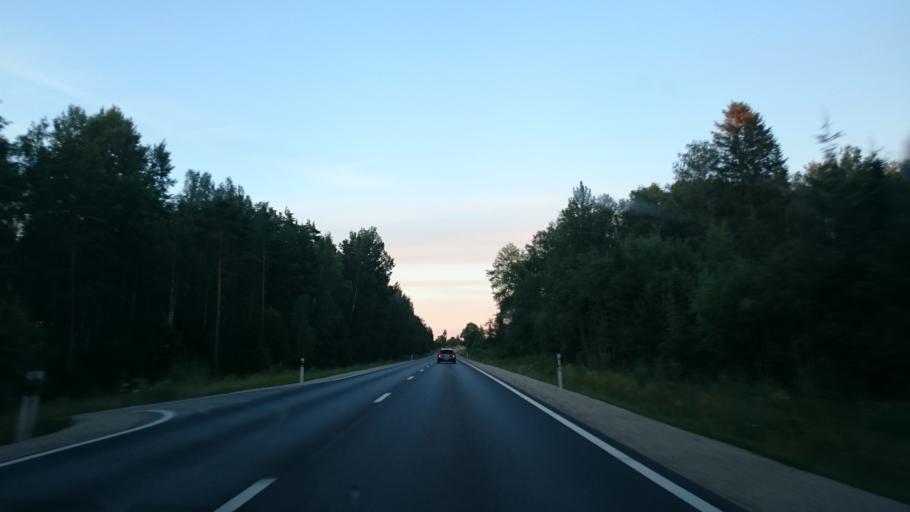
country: LV
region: Jaunpils
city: Jaunpils
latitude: 56.6970
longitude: 23.1454
